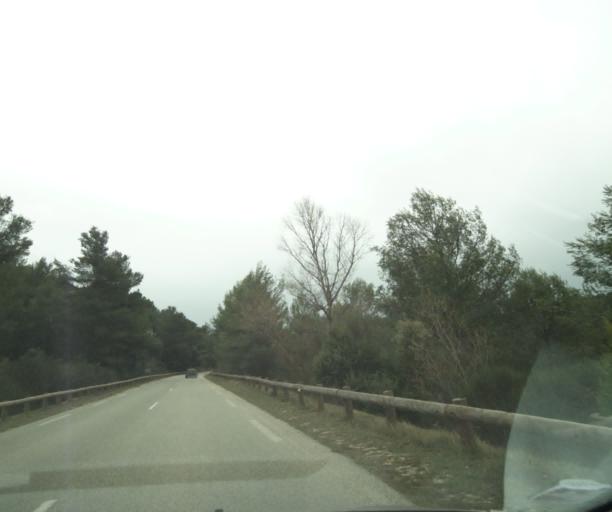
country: FR
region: Provence-Alpes-Cote d'Azur
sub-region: Departement des Bouches-du-Rhone
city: Saint-Marc-Jaumegarde
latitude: 43.5537
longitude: 5.5441
